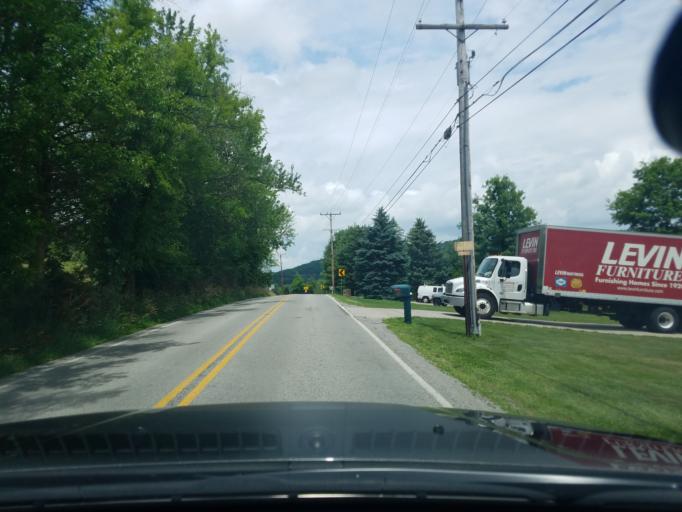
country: US
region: Pennsylvania
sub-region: Westmoreland County
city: Youngwood
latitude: 40.2159
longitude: -79.5392
